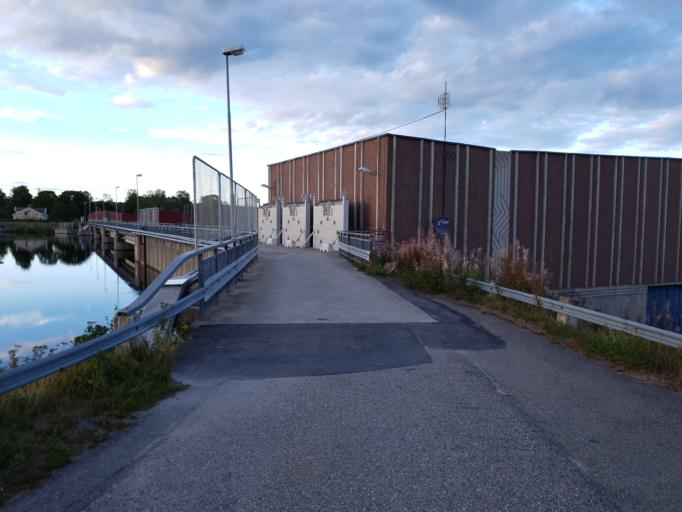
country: SE
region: Gaevleborg
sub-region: Soderhamns Kommun
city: Ljusne
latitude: 61.2058
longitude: 17.1203
